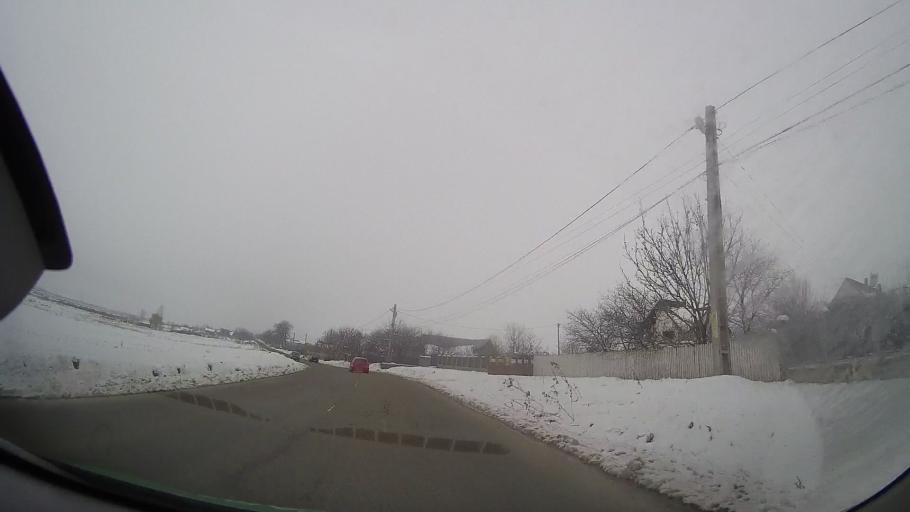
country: RO
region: Vaslui
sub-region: Comuna Negresti
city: Negresti
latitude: 46.8393
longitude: 27.4325
